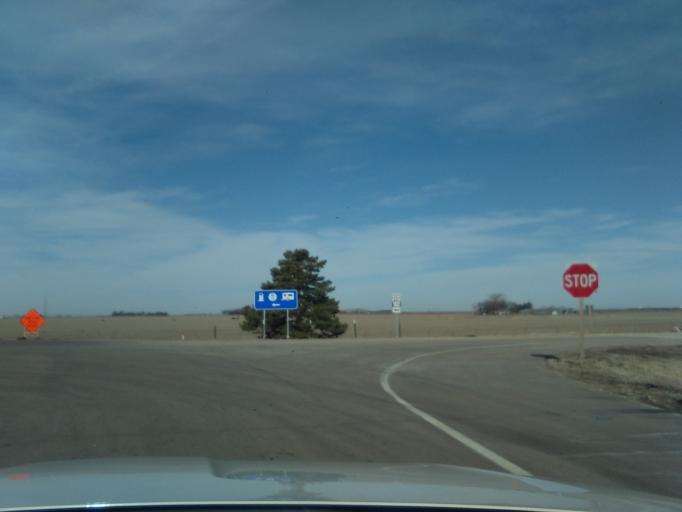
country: US
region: Nebraska
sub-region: Saline County
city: Friend
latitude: 40.8238
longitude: -97.2917
